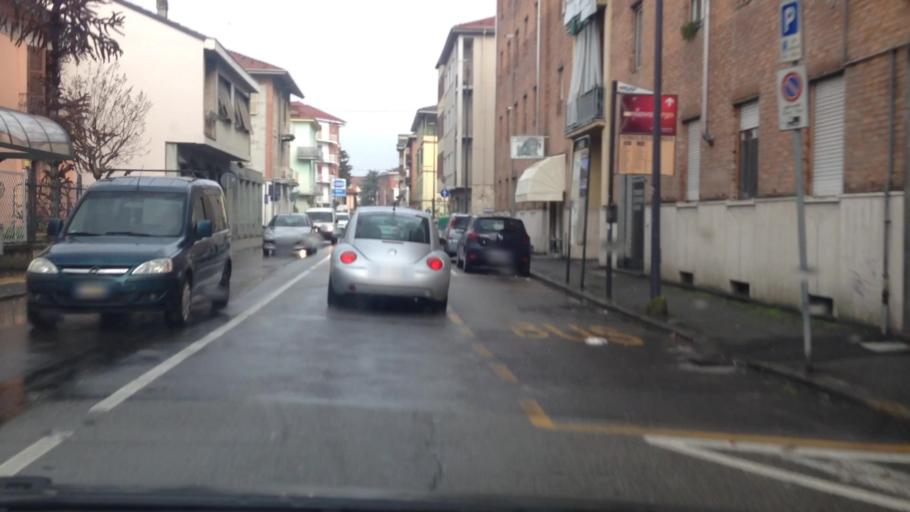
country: IT
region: Piedmont
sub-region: Provincia di Asti
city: Asti
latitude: 44.9058
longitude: 8.2137
